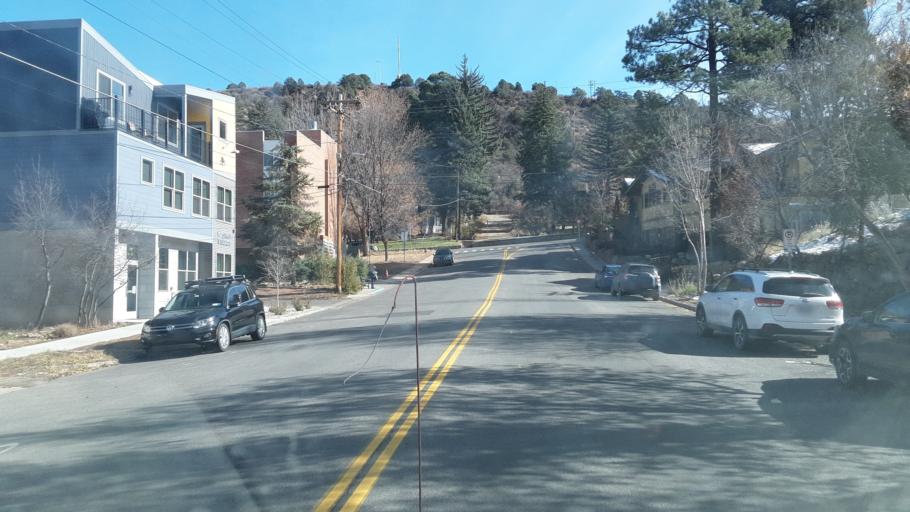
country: US
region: Colorado
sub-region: La Plata County
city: Durango
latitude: 37.2783
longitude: -107.8773
